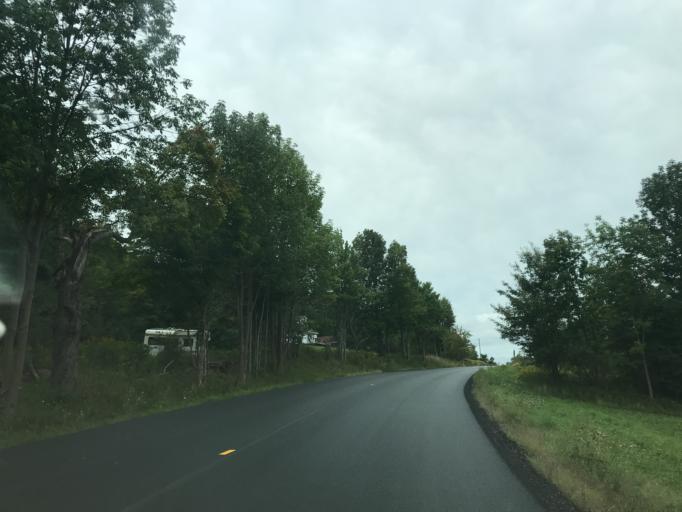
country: US
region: New York
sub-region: Delaware County
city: Stamford
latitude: 42.5159
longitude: -74.6256
